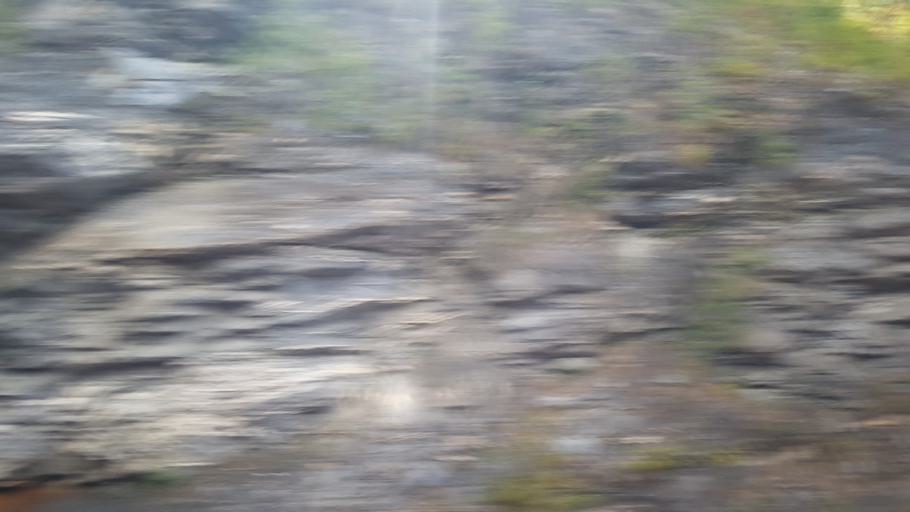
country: NO
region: Sor-Trondelag
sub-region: Rennebu
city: Berkak
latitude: 62.9100
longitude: 10.1299
